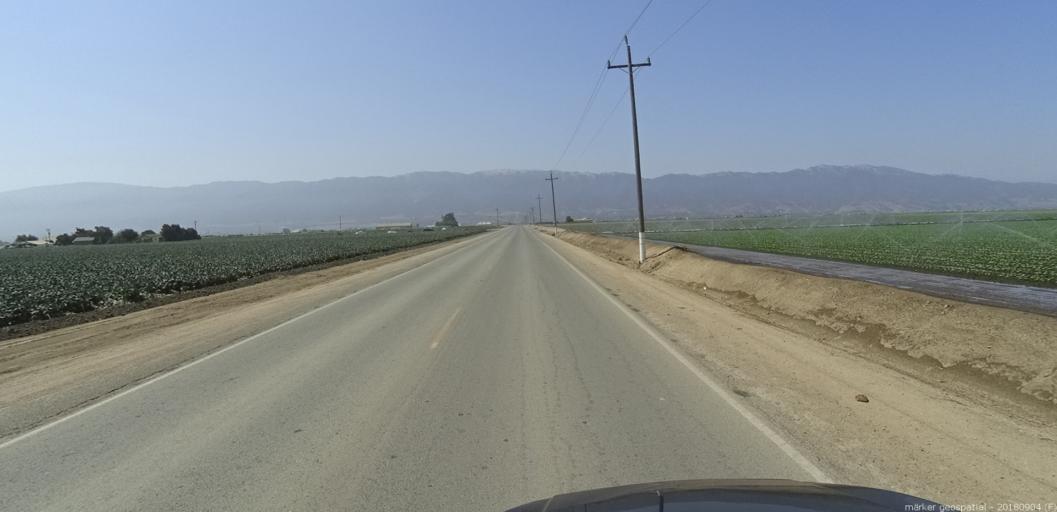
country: US
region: California
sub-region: Monterey County
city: Gonzales
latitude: 36.5348
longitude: -121.4660
